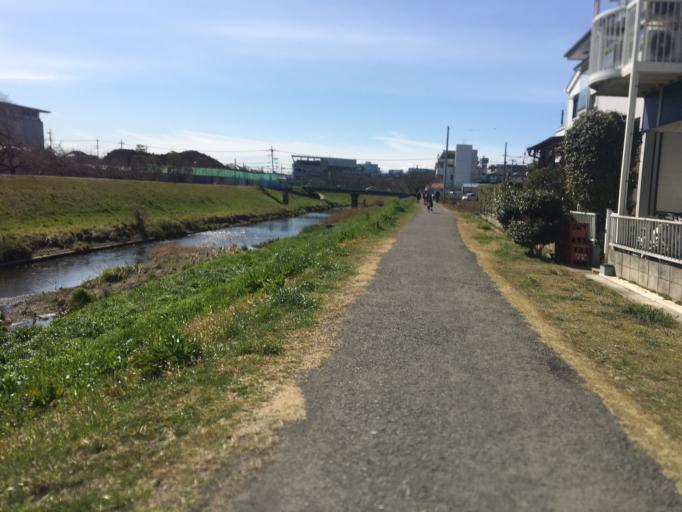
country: JP
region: Saitama
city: Asaka
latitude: 35.8161
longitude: 139.5932
